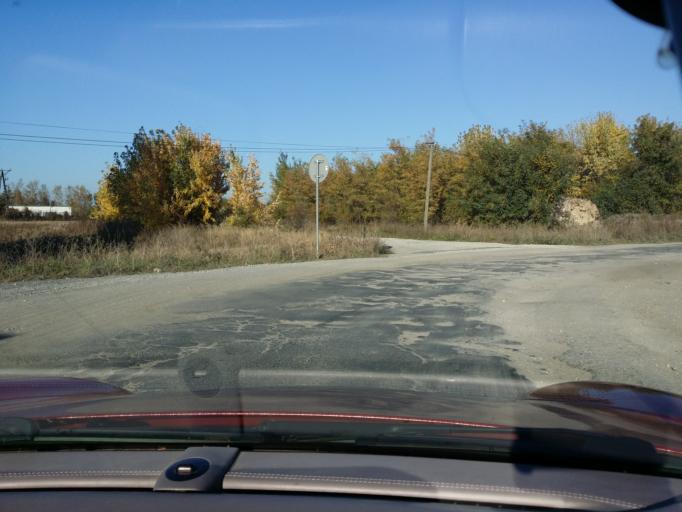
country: PL
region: Masovian Voivodeship
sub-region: Powiat szydlowiecki
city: Mirow
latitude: 51.2445
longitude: 21.0109
